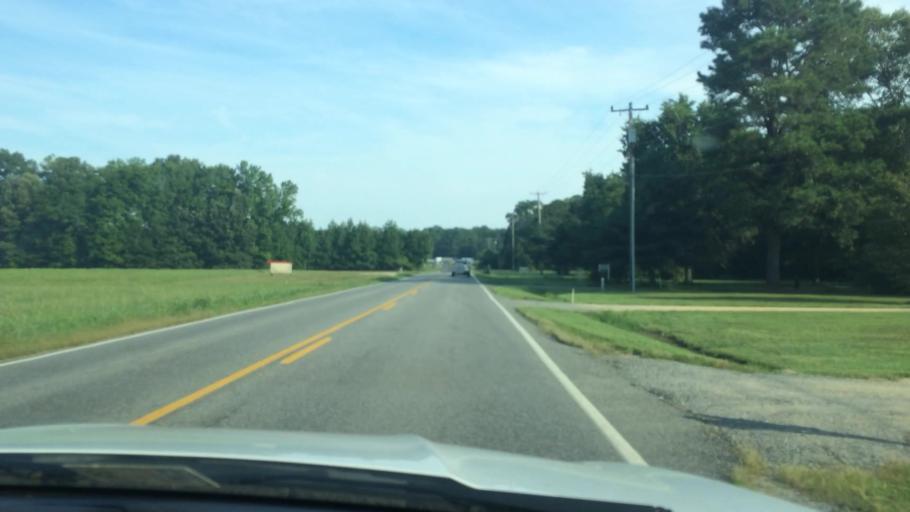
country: US
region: Virginia
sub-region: Middlesex County
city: Deltaville
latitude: 37.4985
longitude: -76.4126
